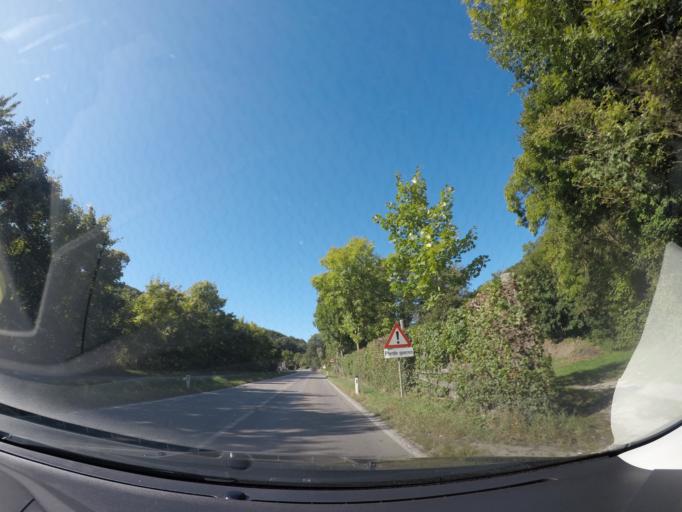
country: AT
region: Lower Austria
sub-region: Politischer Bezirk Modling
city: Laab im Walde
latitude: 48.1443
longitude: 16.1946
